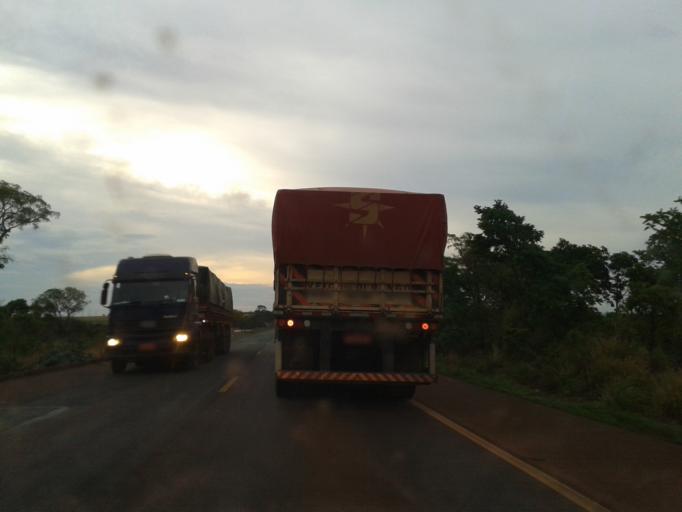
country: BR
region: Goias
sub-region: Santa Helena De Goias
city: Santa Helena de Goias
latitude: -17.9431
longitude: -50.5220
